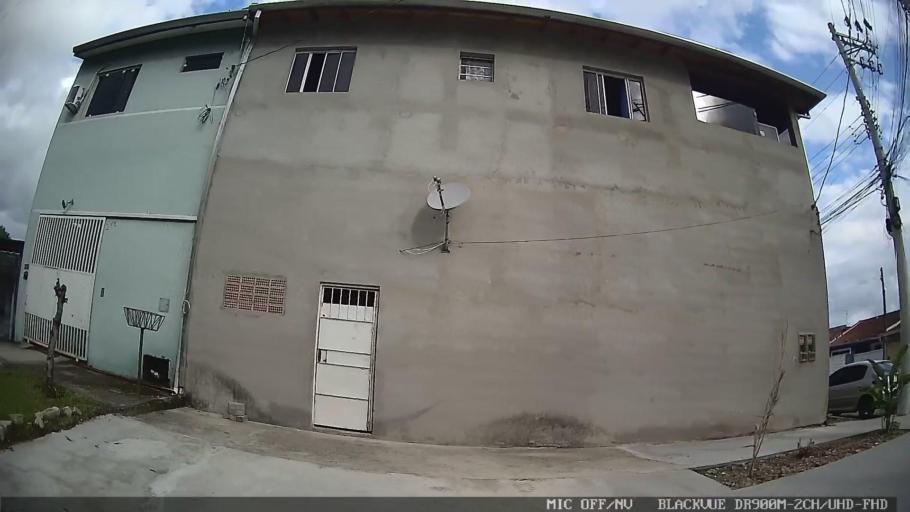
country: BR
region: Sao Paulo
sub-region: Caraguatatuba
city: Caraguatatuba
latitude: -23.6323
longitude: -45.4389
